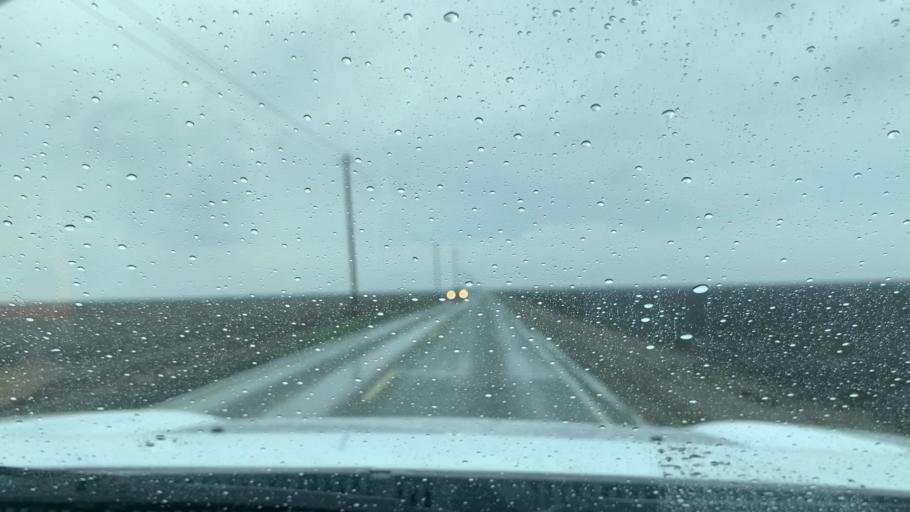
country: US
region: California
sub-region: Tulare County
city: Alpaugh
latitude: 35.9748
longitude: -119.5720
